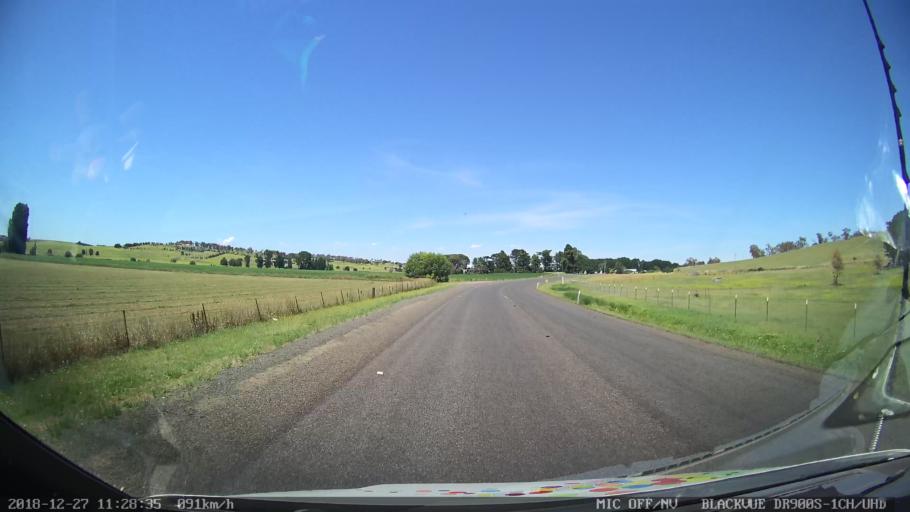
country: AU
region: New South Wales
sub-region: Bathurst Regional
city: Perthville
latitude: -33.4782
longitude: 149.5626
